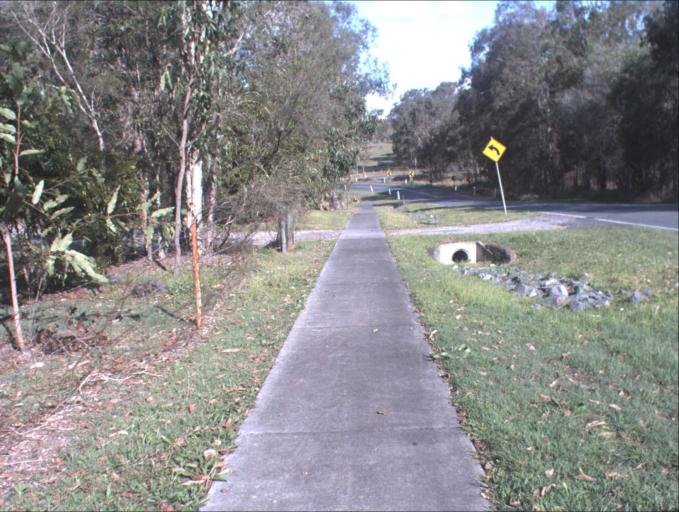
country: AU
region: Queensland
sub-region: Logan
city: Chambers Flat
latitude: -27.7624
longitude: 153.0926
